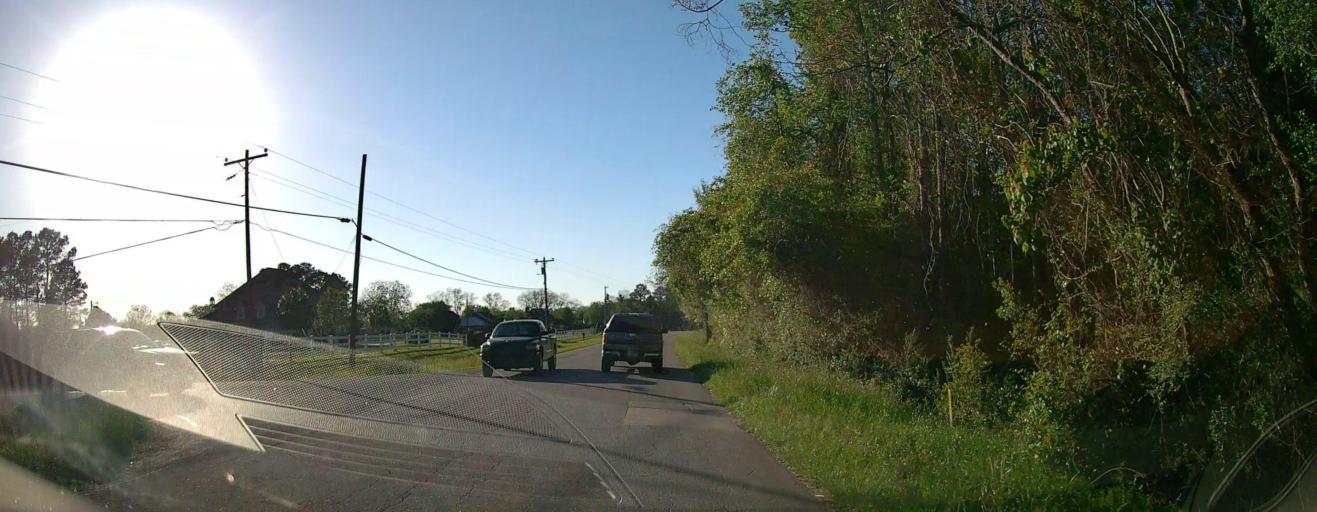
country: US
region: Georgia
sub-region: Ben Hill County
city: Fitzgerald
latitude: 31.7021
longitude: -83.2253
